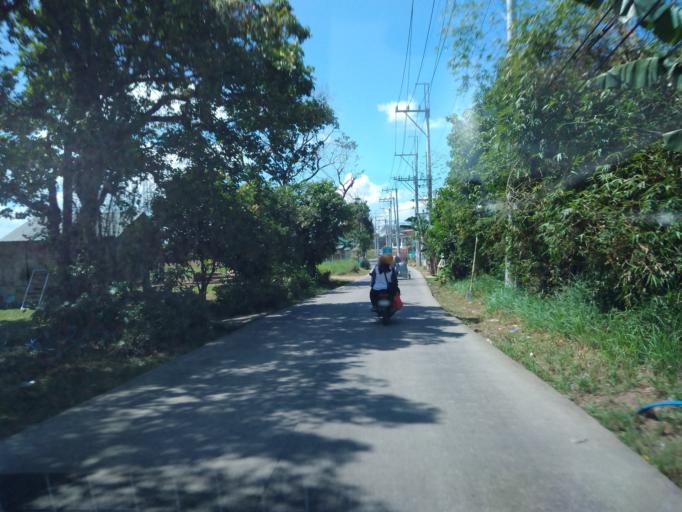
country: PH
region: Central Luzon
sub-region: Province of Bulacan
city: Balasing
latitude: 14.8588
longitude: 121.0220
